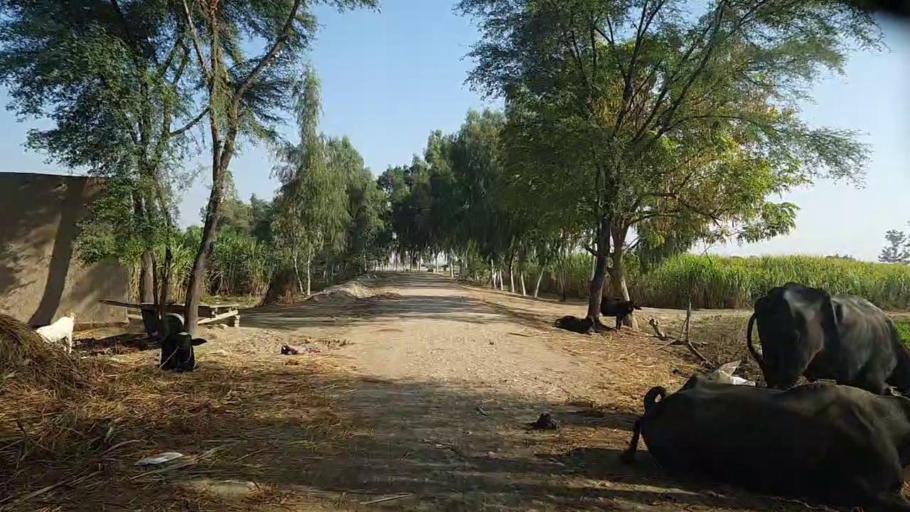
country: PK
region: Sindh
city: Darya Khan Marri
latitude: 26.6533
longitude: 68.3583
